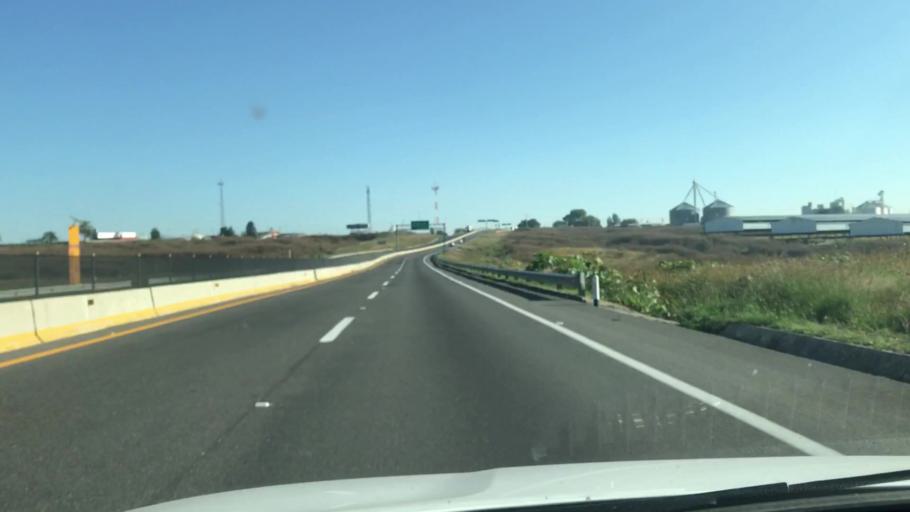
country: MX
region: Jalisco
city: San Juan de los Lagos
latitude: 21.2841
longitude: -102.2727
